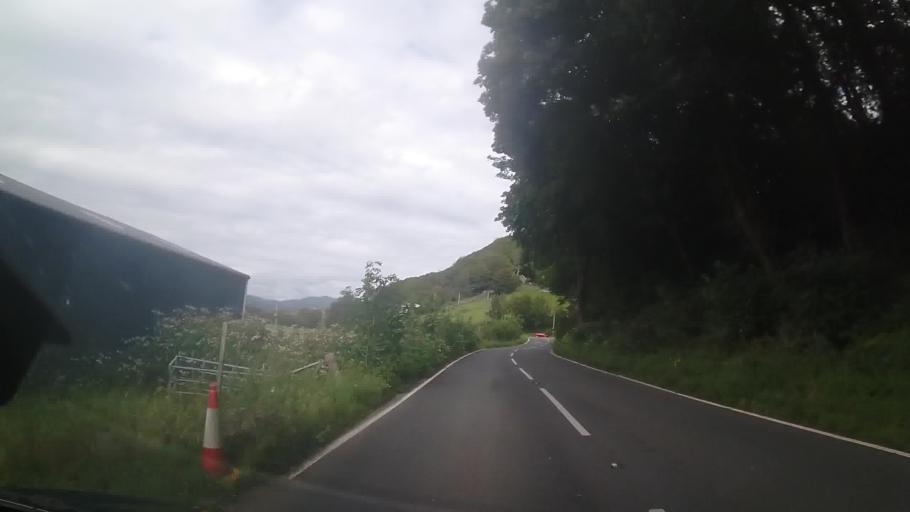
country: GB
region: Wales
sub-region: Gwynedd
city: Barmouth
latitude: 52.7068
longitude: -4.0203
